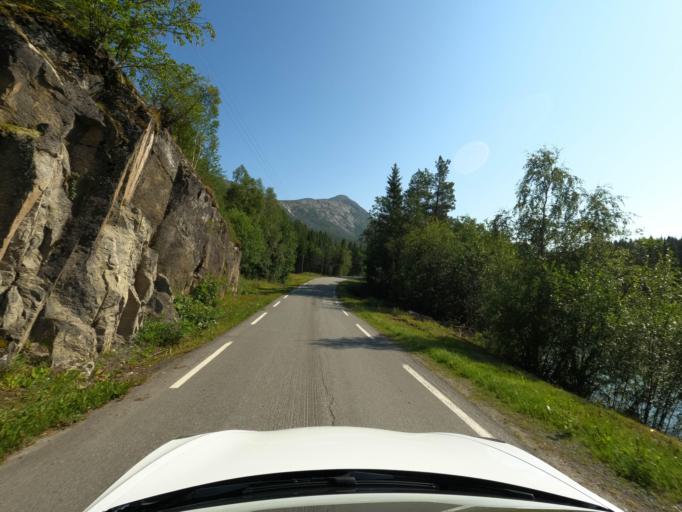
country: NO
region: Nordland
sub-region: Narvik
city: Narvik
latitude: 68.2008
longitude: 17.5466
